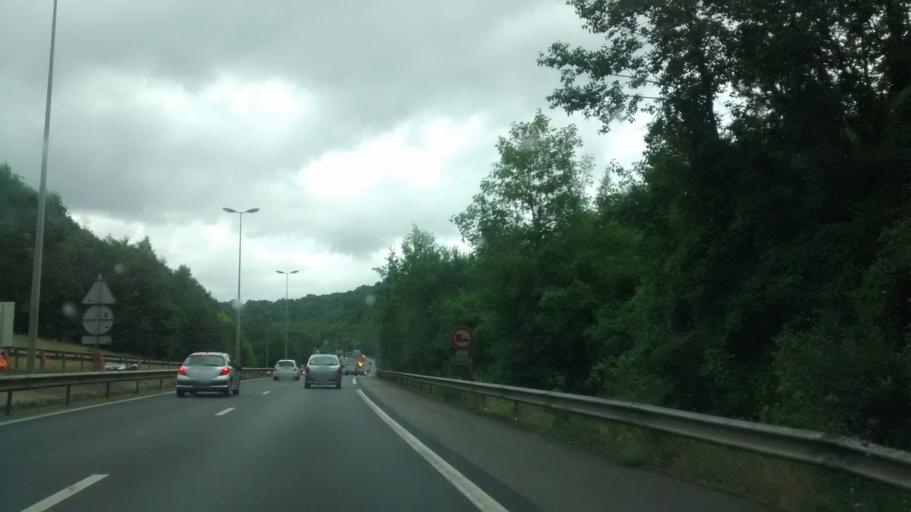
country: FR
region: Haute-Normandie
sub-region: Departement de la Seine-Maritime
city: Darnetal
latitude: 49.4538
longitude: 1.1449
